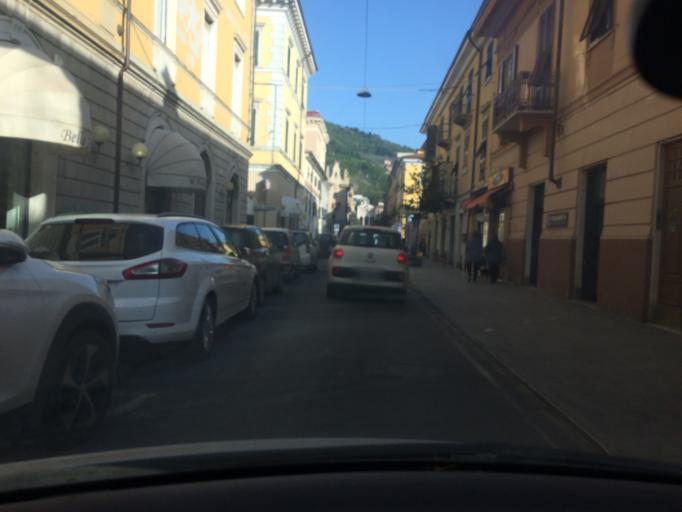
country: IT
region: Tuscany
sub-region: Provincia di Massa-Carrara
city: Carrara
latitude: 44.0775
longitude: 10.1001
